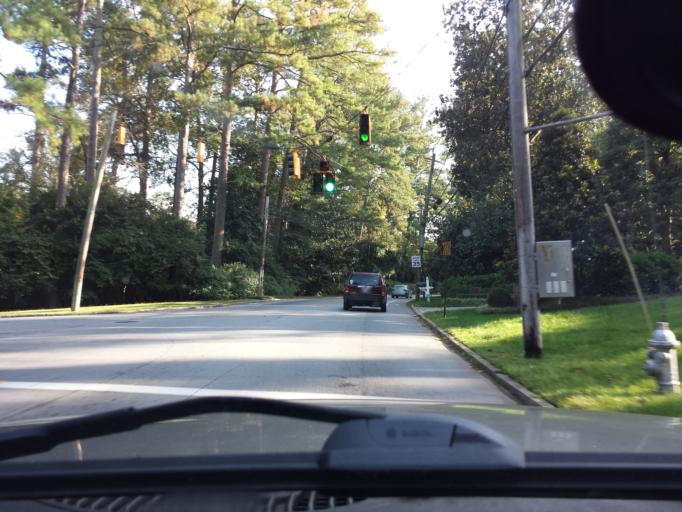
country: US
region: Georgia
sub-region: Cobb County
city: Vinings
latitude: 33.8601
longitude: -84.4035
